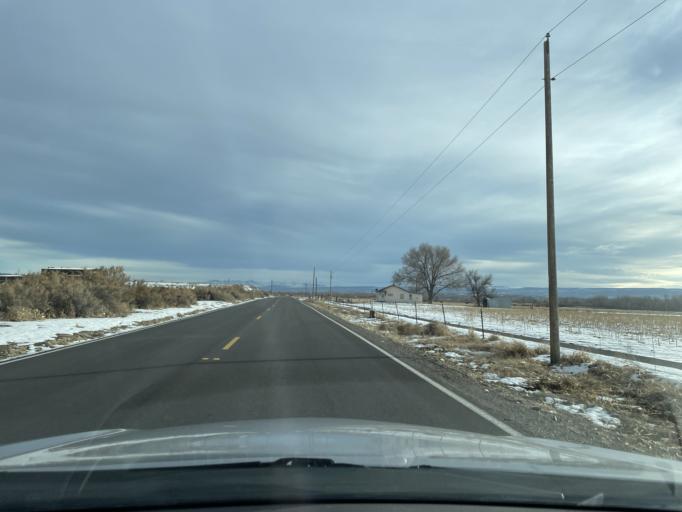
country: US
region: Colorado
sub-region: Montrose County
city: Olathe
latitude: 38.6601
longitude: -107.9980
